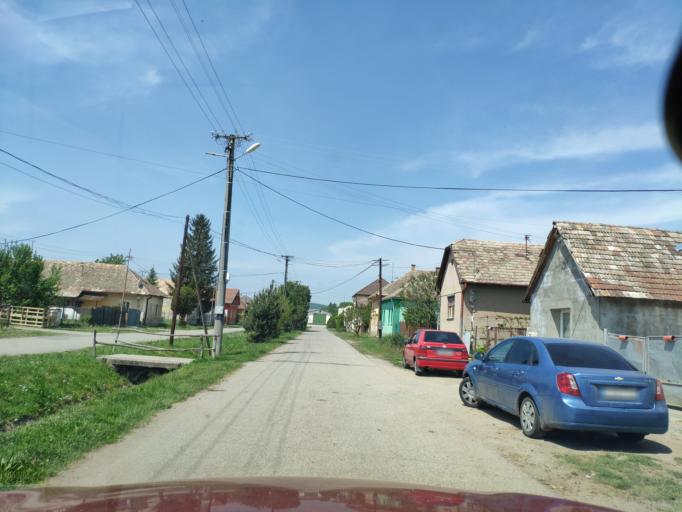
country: SK
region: Banskobystricky
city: Rimavska Sobota
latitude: 48.4456
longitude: 20.1164
